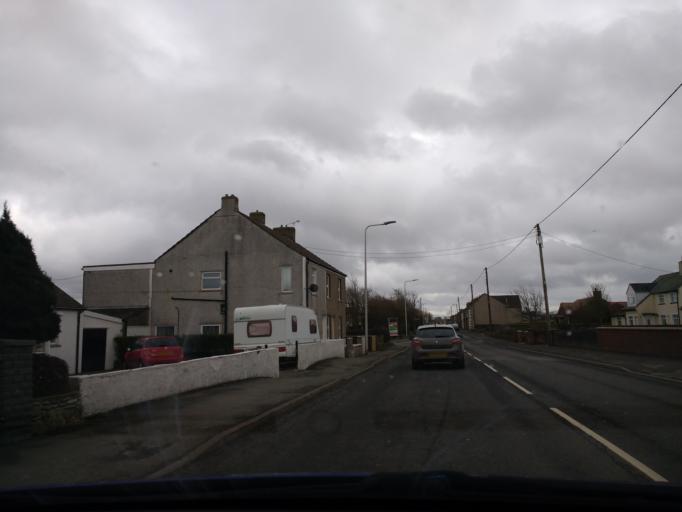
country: GB
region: England
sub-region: Cumbria
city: Dearham
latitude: 54.7040
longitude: -3.4507
